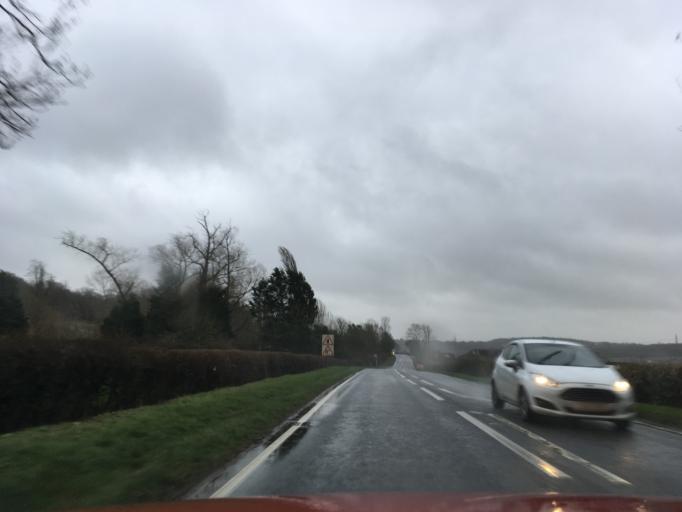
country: GB
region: England
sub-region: Oxfordshire
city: Eynsham
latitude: 51.7576
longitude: -1.3391
